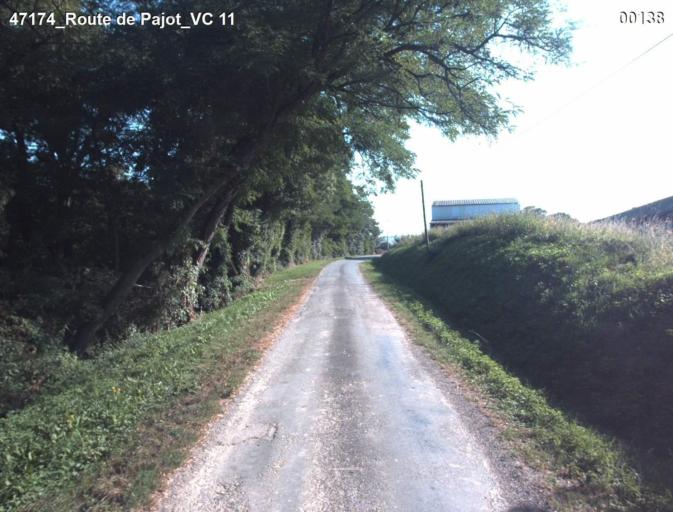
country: FR
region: Aquitaine
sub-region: Departement du Lot-et-Garonne
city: Nerac
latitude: 44.0815
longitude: 0.3600
